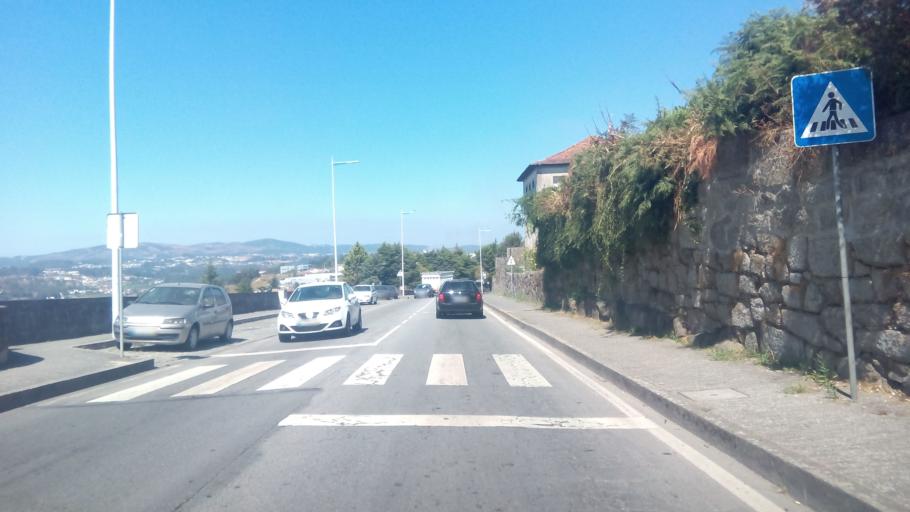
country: PT
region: Porto
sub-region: Penafiel
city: Penafiel
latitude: 41.2078
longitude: -8.2873
